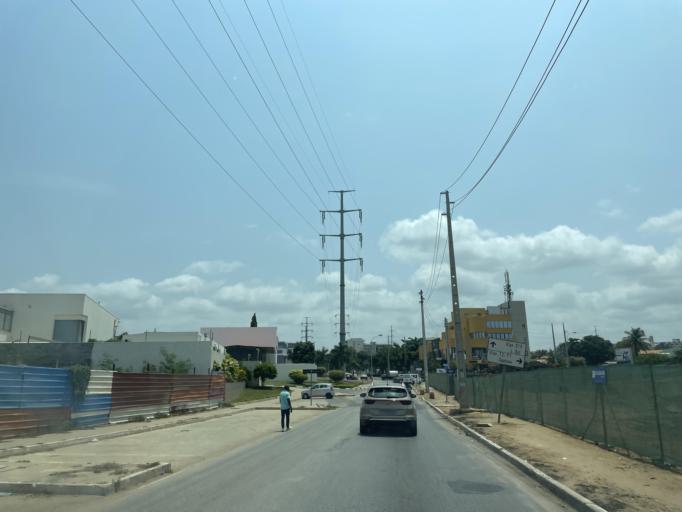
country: AO
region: Luanda
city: Luanda
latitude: -8.9072
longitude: 13.1944
